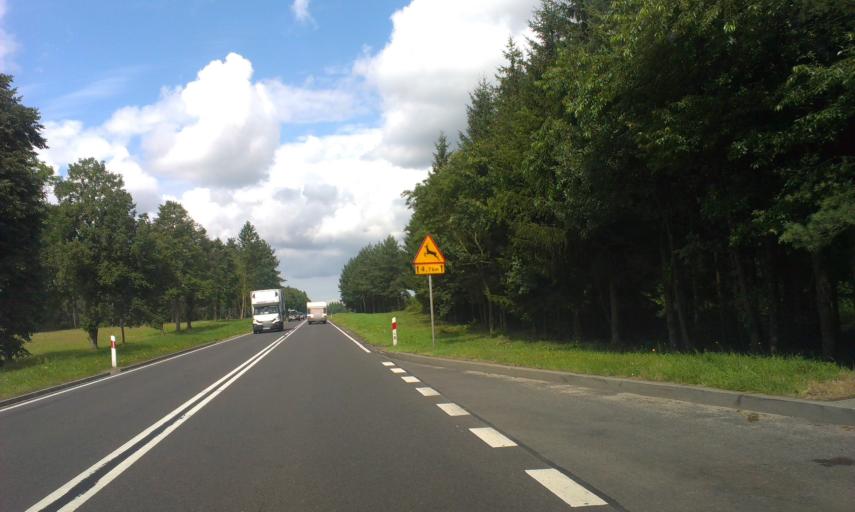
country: PL
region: West Pomeranian Voivodeship
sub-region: Powiat koszalinski
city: Sianow
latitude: 54.0923
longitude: 16.3659
